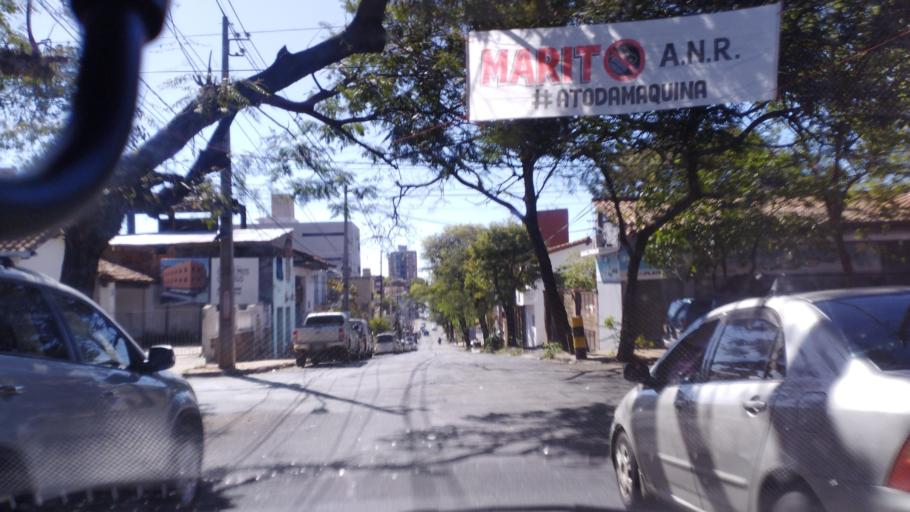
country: PY
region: Asuncion
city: Asuncion
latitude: -25.2936
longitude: -57.6192
